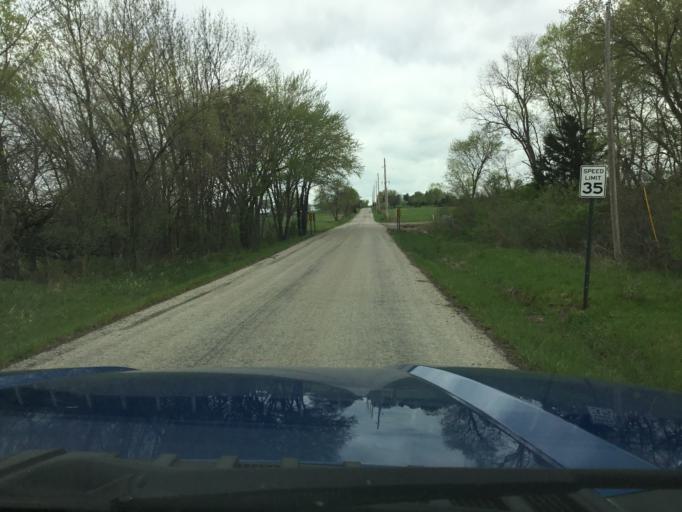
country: US
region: Kansas
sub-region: Douglas County
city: Lawrence
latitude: 38.9289
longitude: -95.1861
